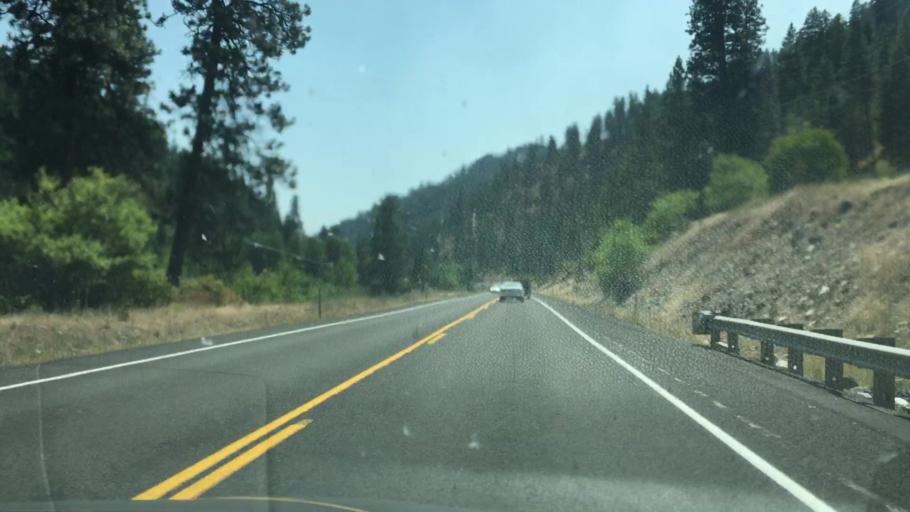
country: US
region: Idaho
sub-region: Valley County
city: McCall
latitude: 45.2101
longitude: -116.3131
